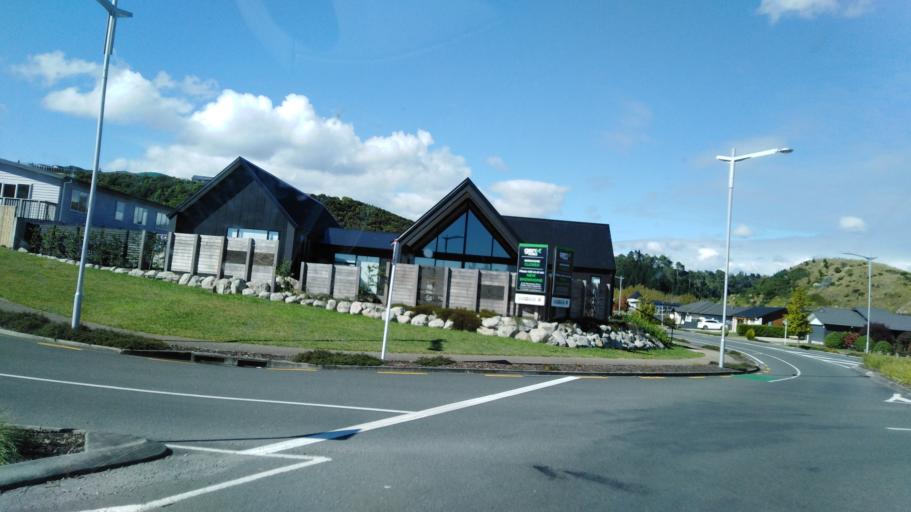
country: NZ
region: Bay of Plenty
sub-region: Tauranga City
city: Tauranga
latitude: -37.7538
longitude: 176.1042
